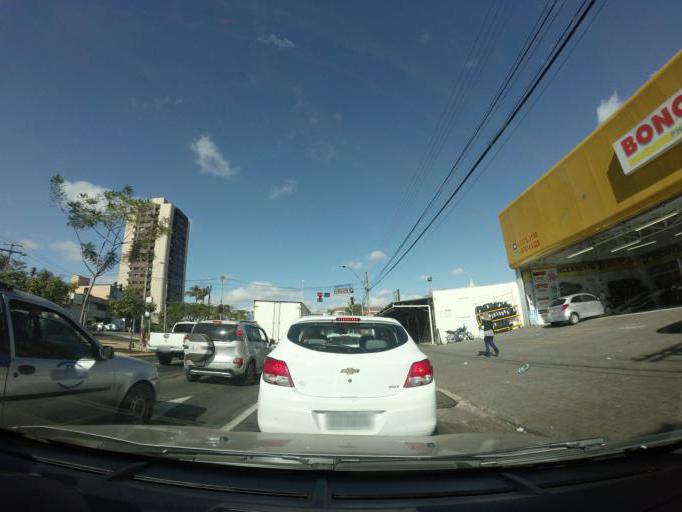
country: BR
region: Sao Paulo
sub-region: Piracicaba
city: Piracicaba
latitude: -22.7139
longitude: -47.6245
